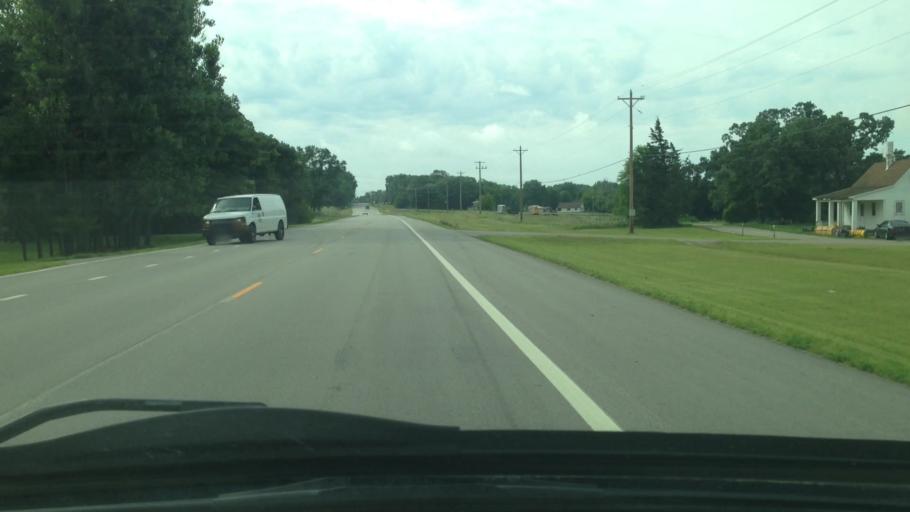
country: US
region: Minnesota
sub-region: Olmsted County
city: Rochester
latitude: 43.9822
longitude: -92.4008
